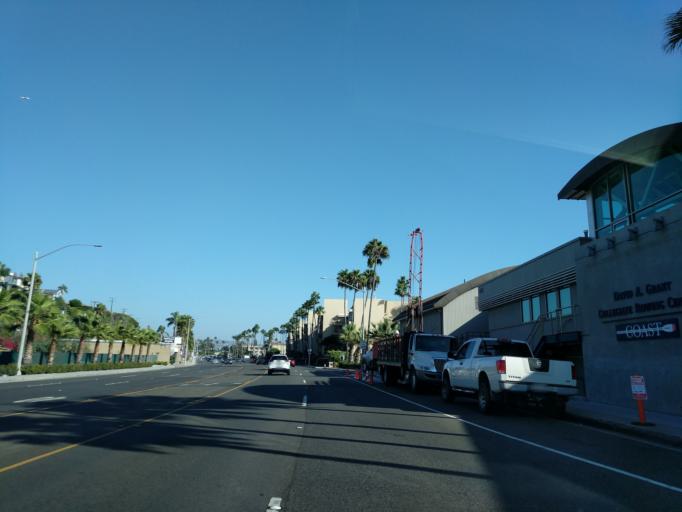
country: US
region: California
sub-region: Orange County
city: Newport Beach
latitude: 33.6172
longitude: -117.9185
